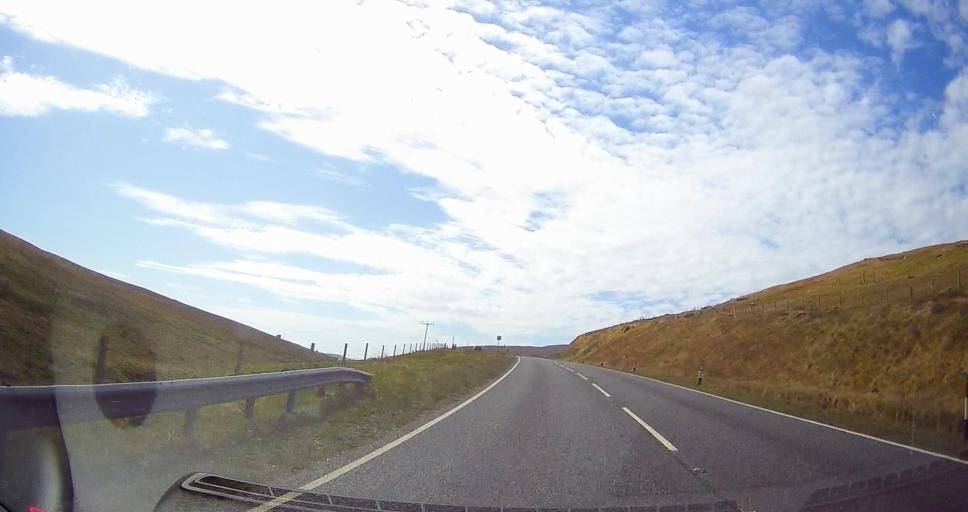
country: GB
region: Scotland
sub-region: Shetland Islands
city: Sandwick
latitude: 60.0030
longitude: -1.2798
